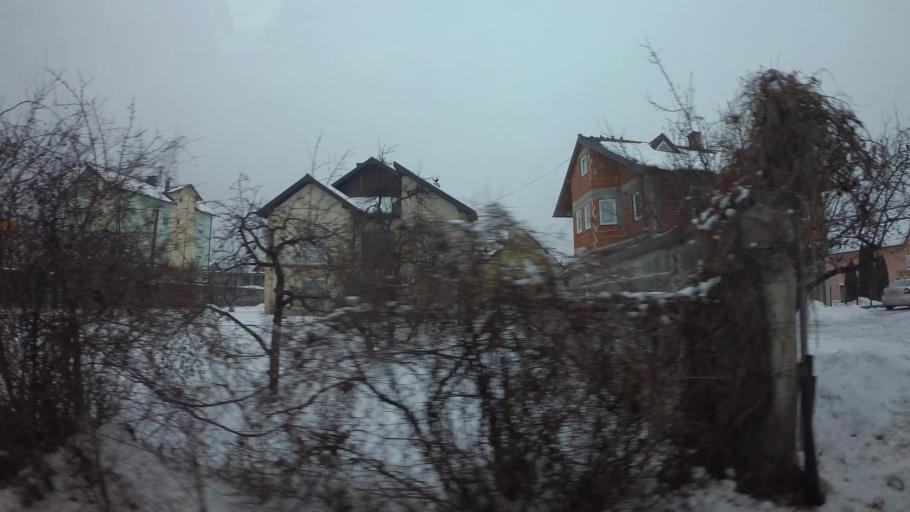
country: BA
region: Federation of Bosnia and Herzegovina
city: Hadzici
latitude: 43.8393
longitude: 18.2765
